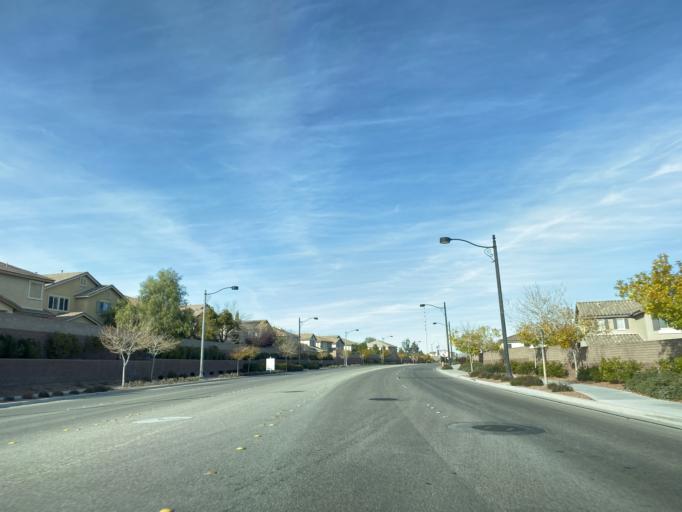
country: US
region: Nevada
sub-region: Clark County
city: Summerlin South
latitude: 36.3042
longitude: -115.3216
